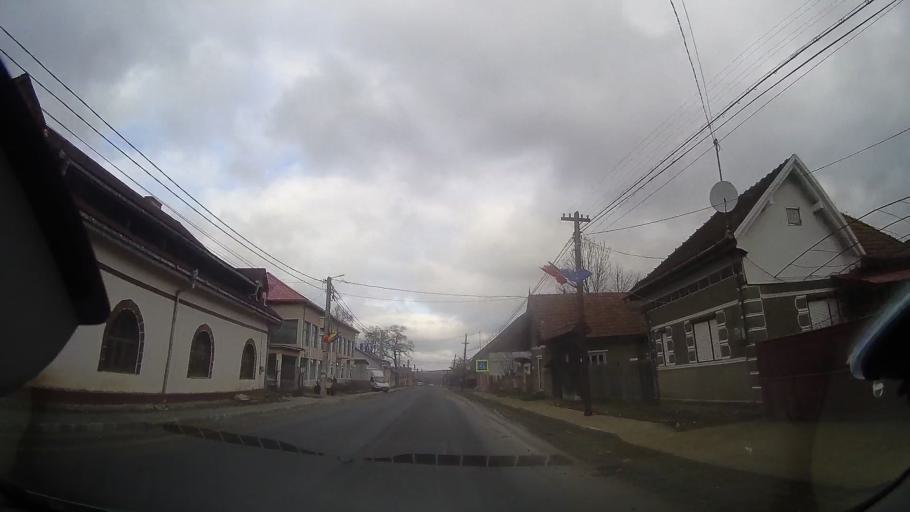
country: RO
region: Cluj
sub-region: Comuna Calatele
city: Calatele
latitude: 46.7654
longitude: 23.0083
